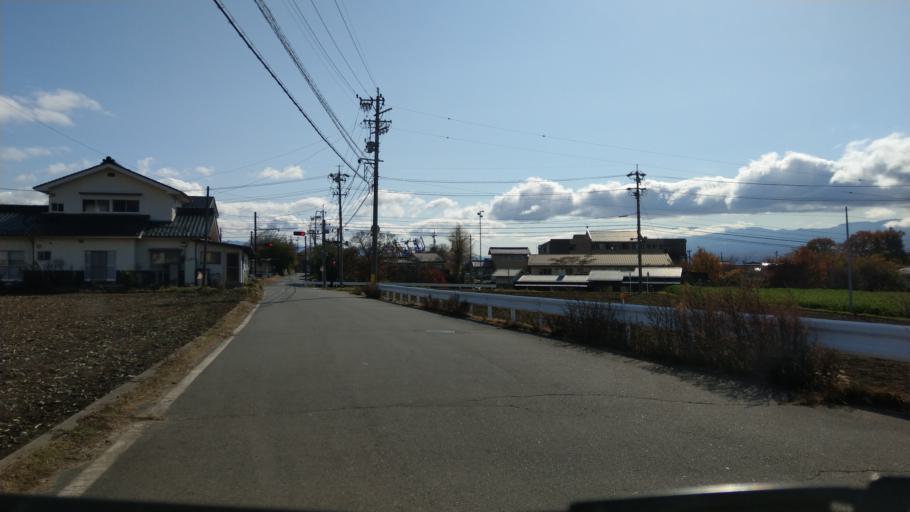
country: JP
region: Nagano
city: Komoro
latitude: 36.3058
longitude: 138.4687
